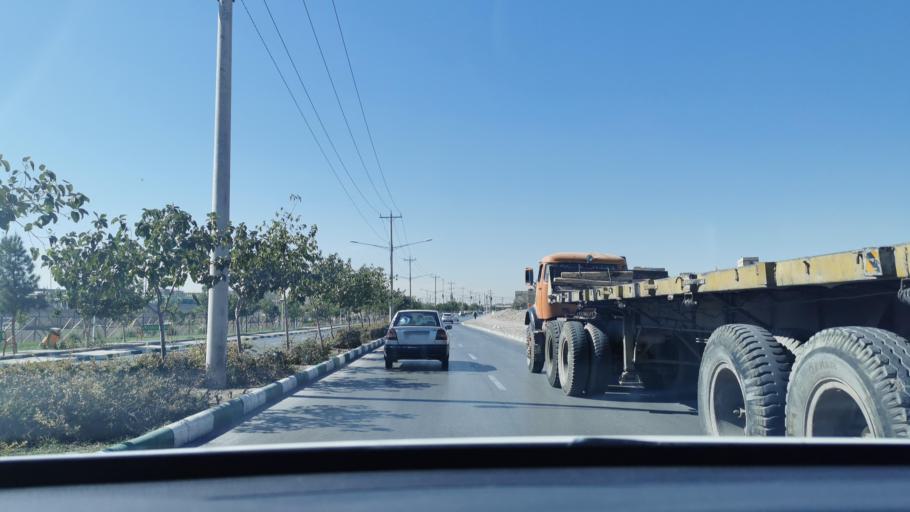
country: IR
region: Razavi Khorasan
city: Mashhad
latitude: 36.3361
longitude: 59.6130
